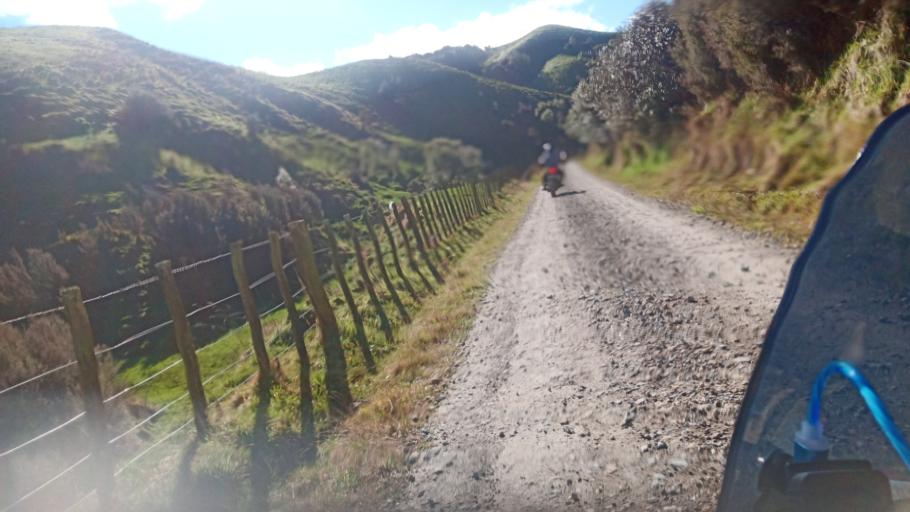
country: NZ
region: Hawke's Bay
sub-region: Wairoa District
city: Wairoa
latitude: -38.6634
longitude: 177.4864
